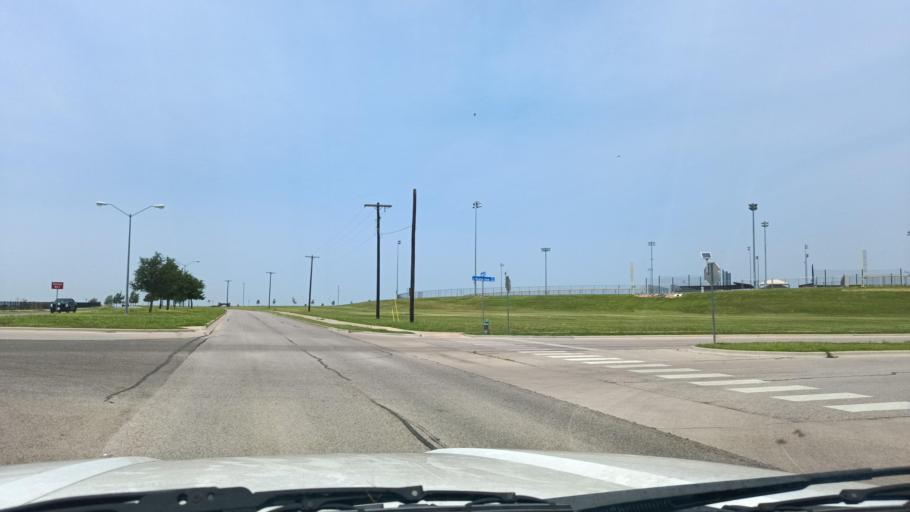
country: US
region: Texas
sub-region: Bell County
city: Morgans Point Resort
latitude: 31.1274
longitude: -97.4069
